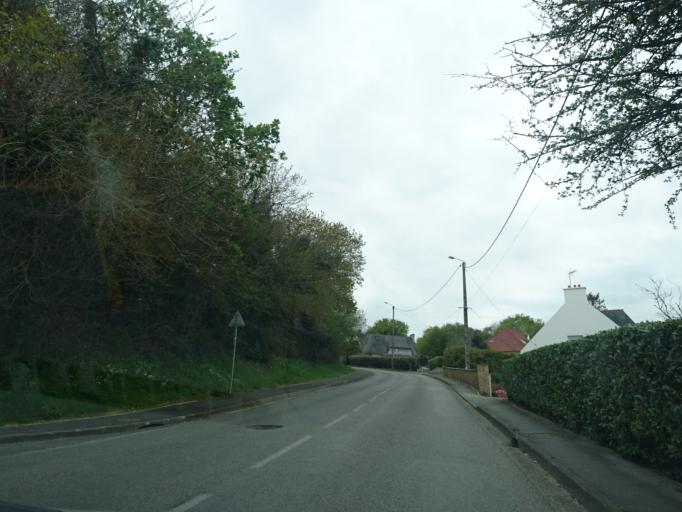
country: FR
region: Brittany
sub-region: Departement du Finistere
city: Roscanvel
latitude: 48.3613
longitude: -4.5551
